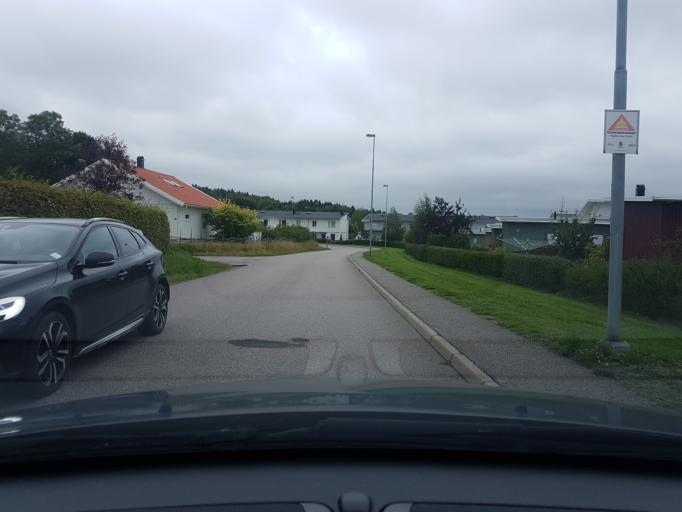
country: SE
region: Vaestra Goetaland
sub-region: Ale Kommun
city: Nodinge-Nol
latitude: 57.8864
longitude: 12.0544
